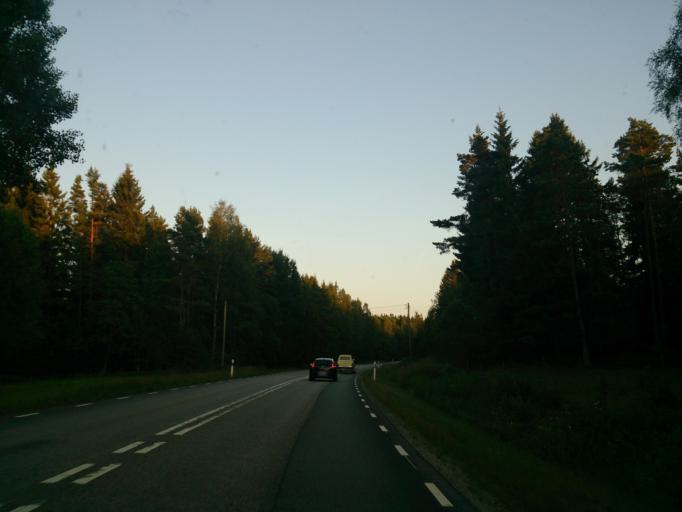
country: SE
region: Joenkoeping
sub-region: Varnamo Kommun
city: Rydaholm
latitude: 56.9230
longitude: 14.4183
